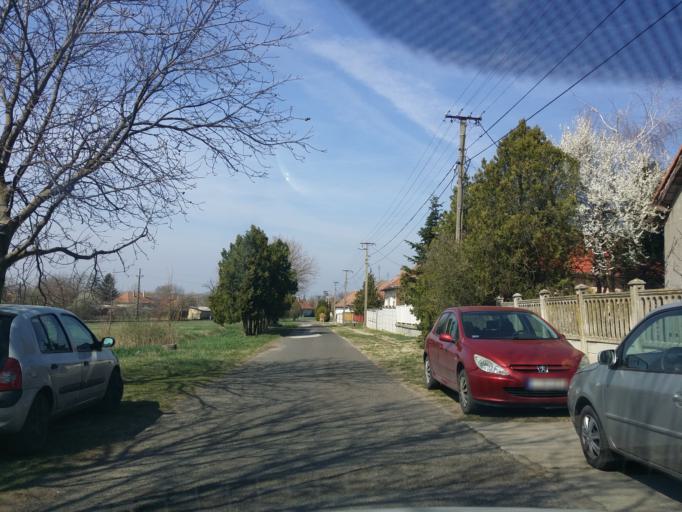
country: HU
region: Pest
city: Cegledbercel
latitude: 47.2269
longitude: 19.6690
